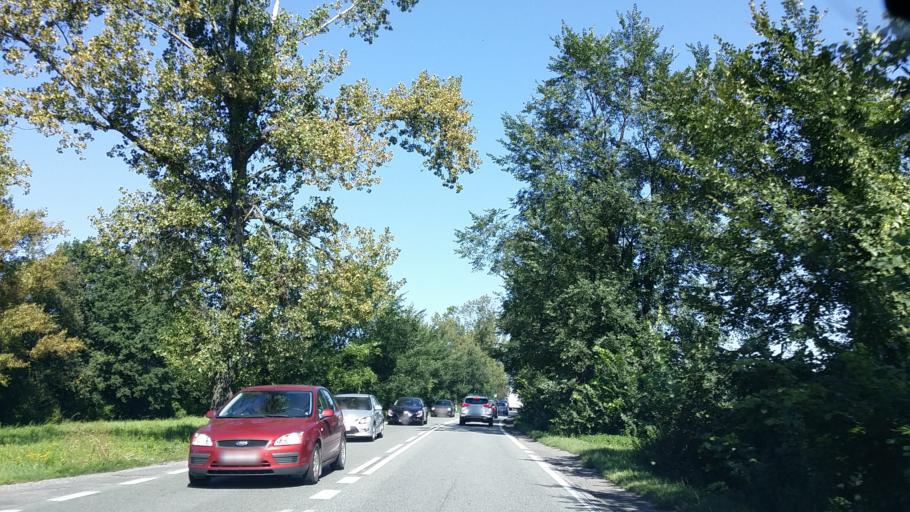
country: PL
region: Lesser Poland Voivodeship
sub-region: Powiat oswiecimski
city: Babice
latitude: 50.0612
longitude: 19.1945
